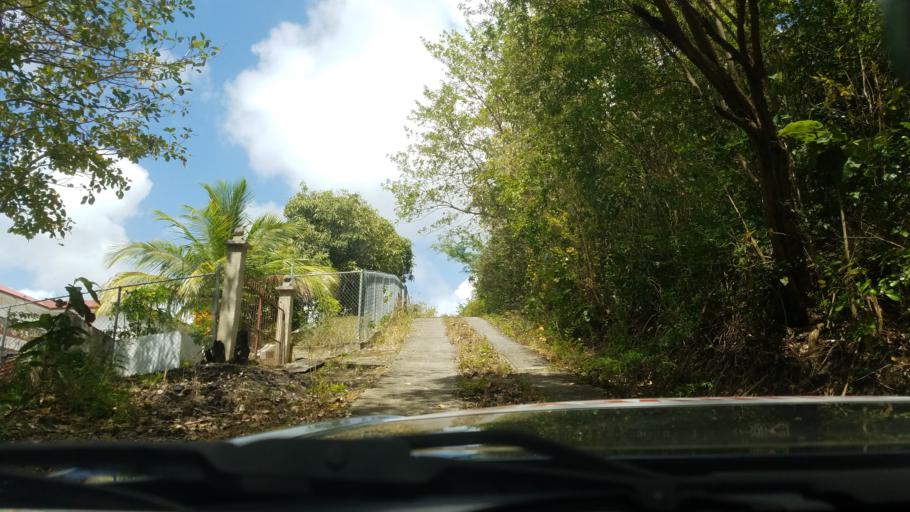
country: LC
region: Gros-Islet
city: Gros Islet
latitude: 14.0636
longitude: -60.9519
